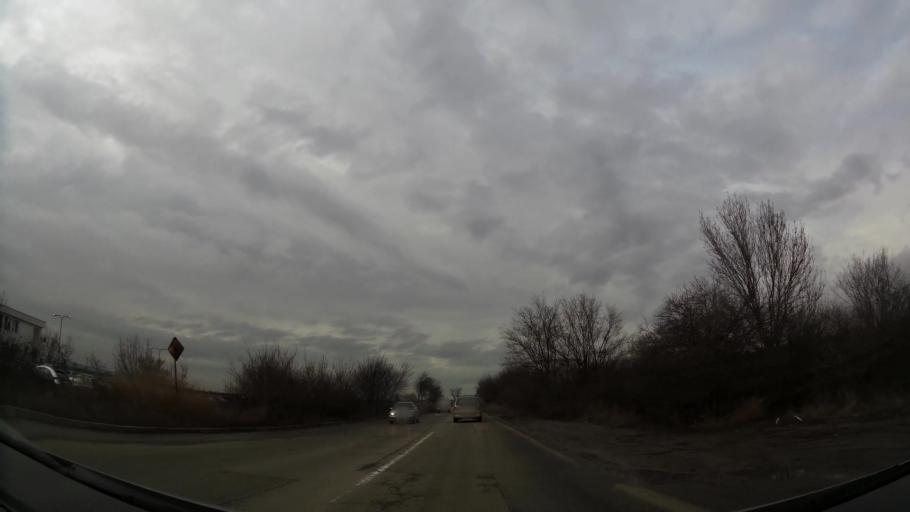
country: BG
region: Sofiya
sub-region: Obshtina Bozhurishte
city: Bozhurishte
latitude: 42.7557
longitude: 23.2712
